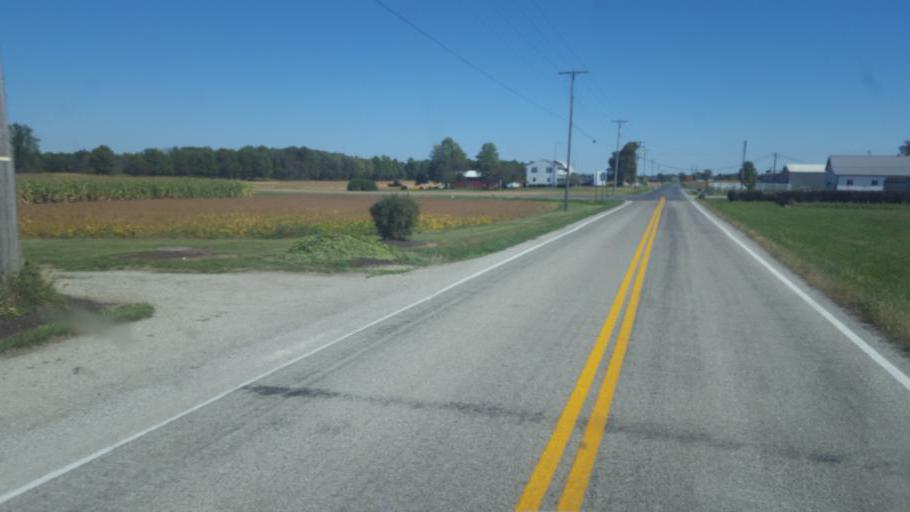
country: US
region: Ohio
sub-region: Huron County
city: Plymouth
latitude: 40.9944
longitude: -82.6071
